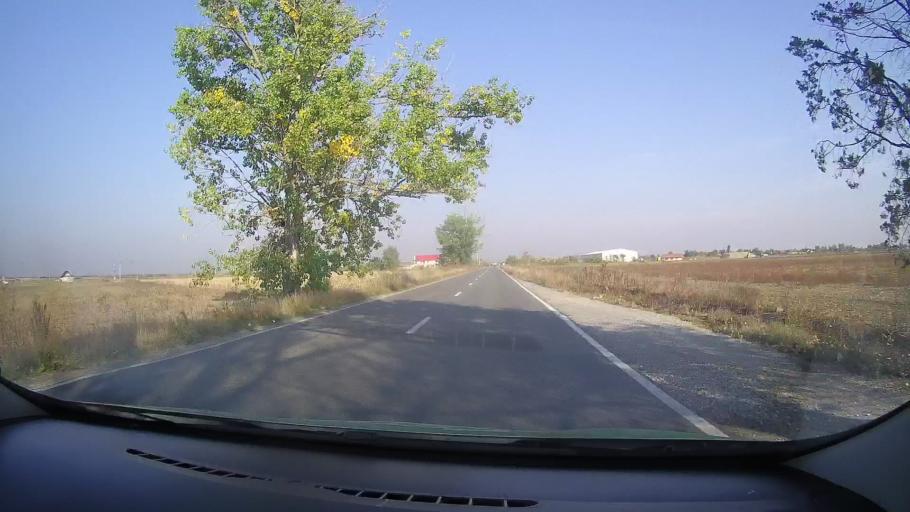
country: RO
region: Arad
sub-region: Comuna Pilu
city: Pilu
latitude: 46.5662
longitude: 21.3447
